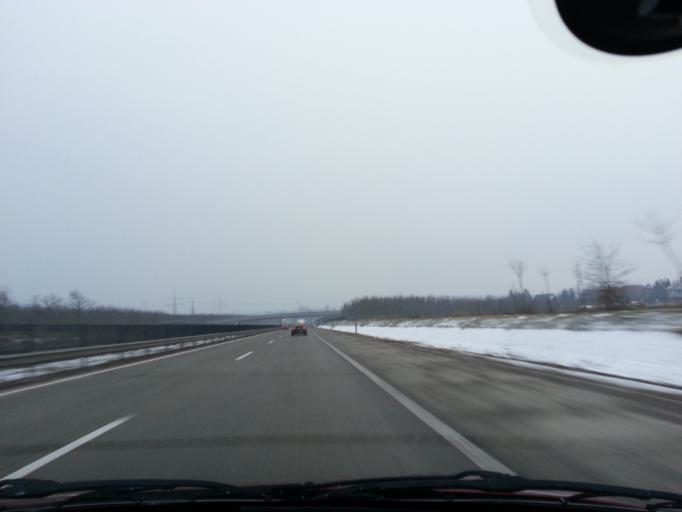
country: HU
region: Pest
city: Ecser
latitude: 47.4484
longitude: 19.3320
